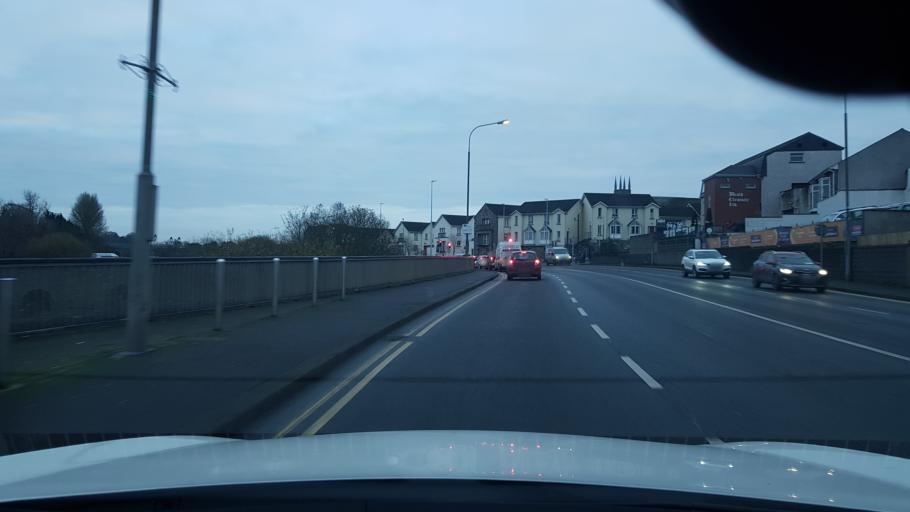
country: IE
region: Leinster
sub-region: An Mhi
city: Navan
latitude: 53.6542
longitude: -6.6822
